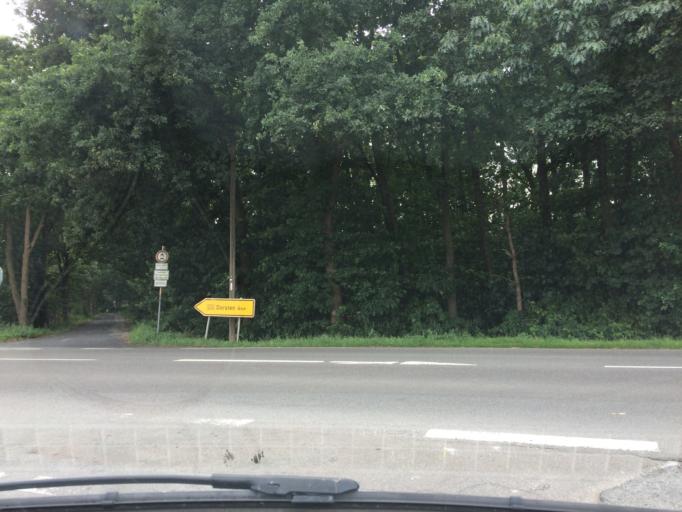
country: DE
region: North Rhine-Westphalia
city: Dorsten
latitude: 51.6893
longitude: 6.9488
